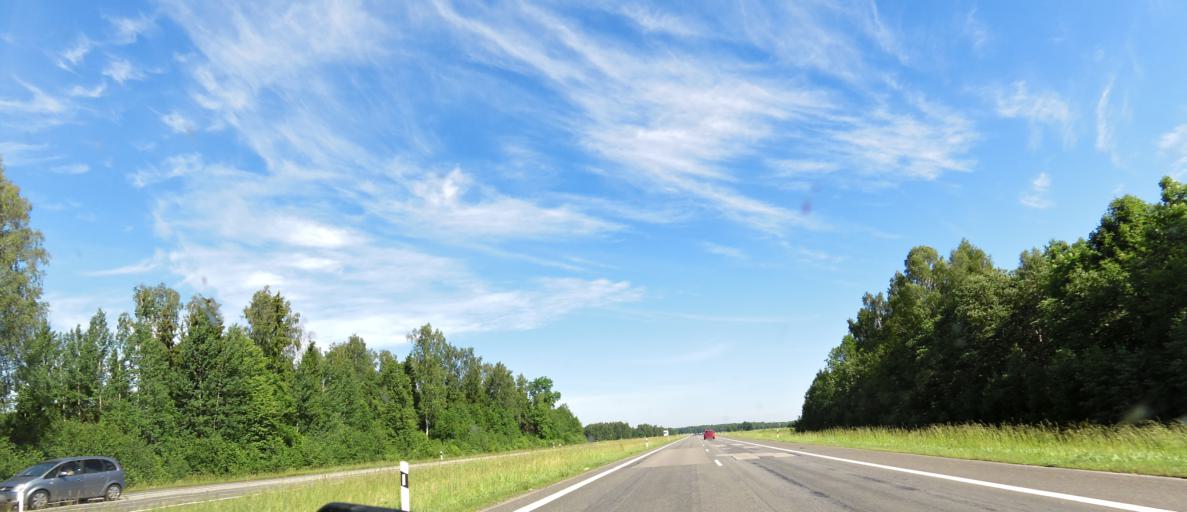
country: LT
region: Vilnius County
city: Ukmerge
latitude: 55.4374
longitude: 24.6738
